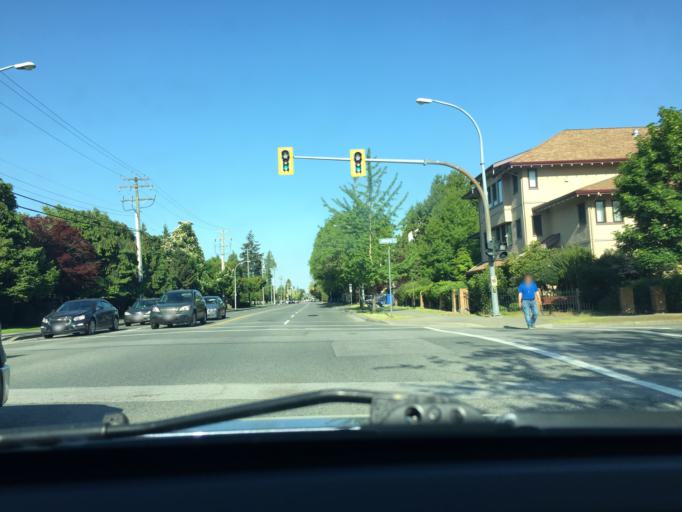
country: CA
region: British Columbia
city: Richmond
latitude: 49.1556
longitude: -123.1402
